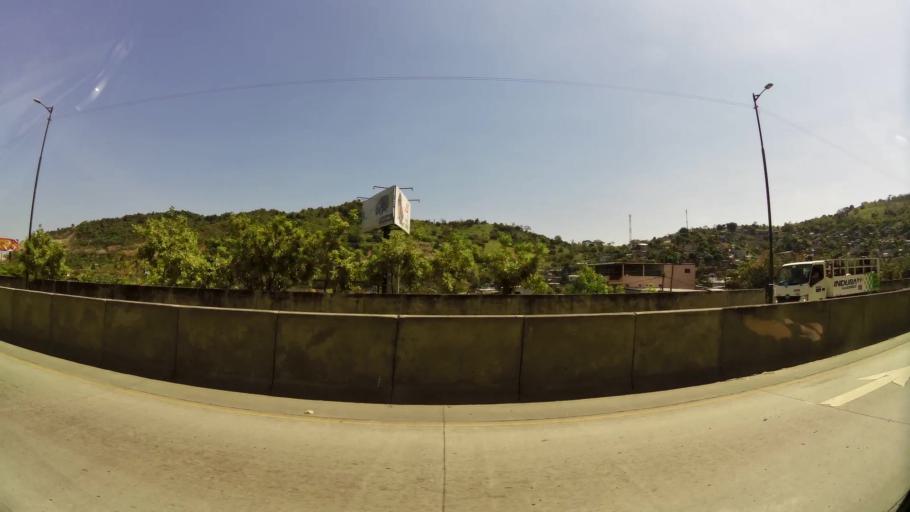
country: EC
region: Guayas
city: Guayaquil
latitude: -2.1803
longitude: -79.9273
